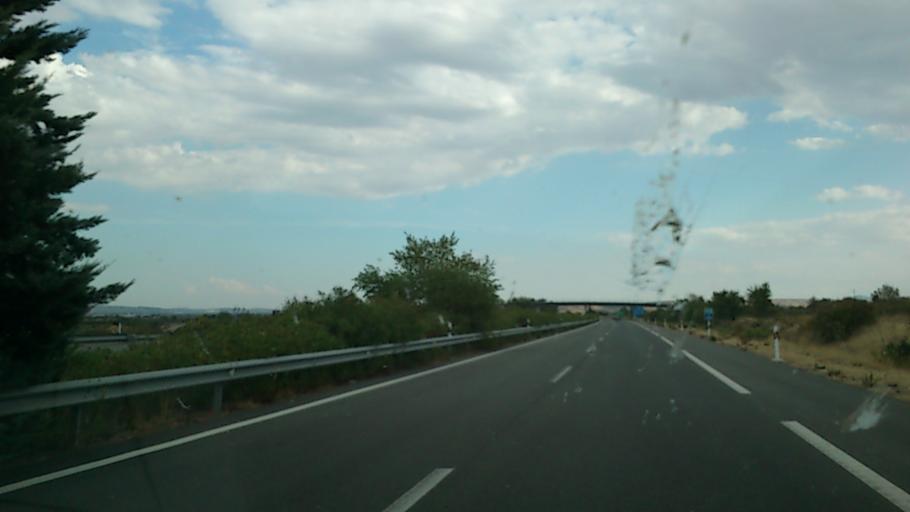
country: ES
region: La Rioja
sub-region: Provincia de La Rioja
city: Pradejon
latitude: 42.3570
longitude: -2.0621
